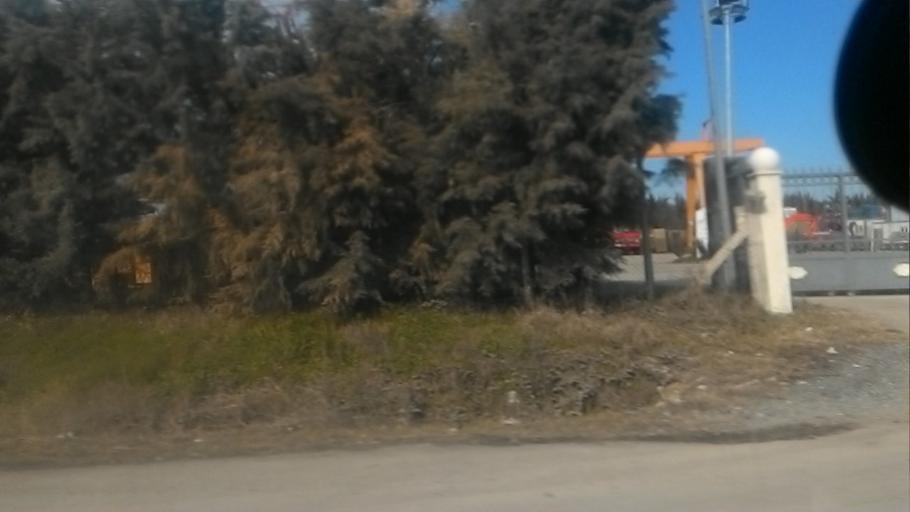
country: TR
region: Istanbul
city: Canta
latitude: 41.0802
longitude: 28.0588
